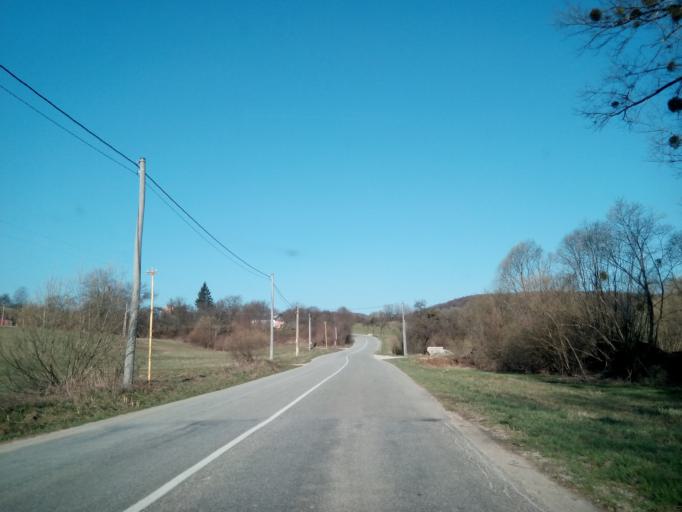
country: SK
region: Kosicky
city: Roznava
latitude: 48.6665
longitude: 20.4320
